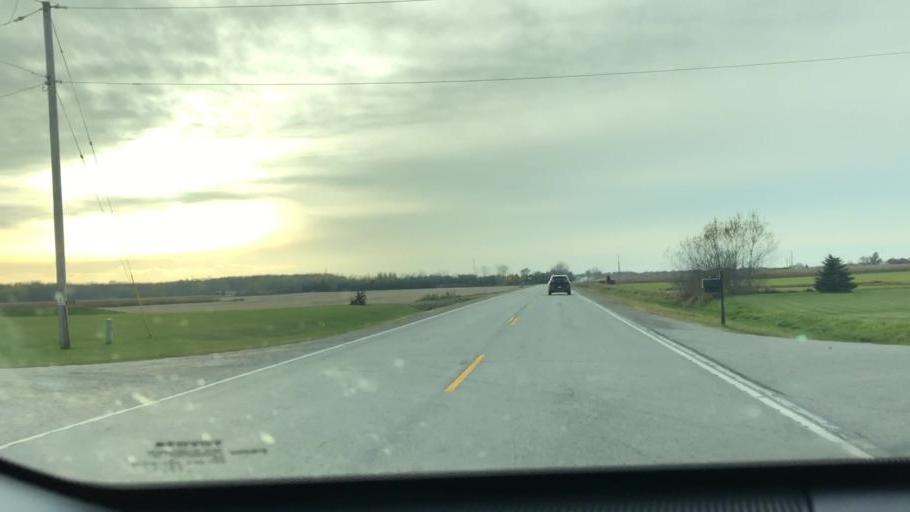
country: US
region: Wisconsin
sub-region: Outagamie County
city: Seymour
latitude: 44.4435
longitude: -88.3369
